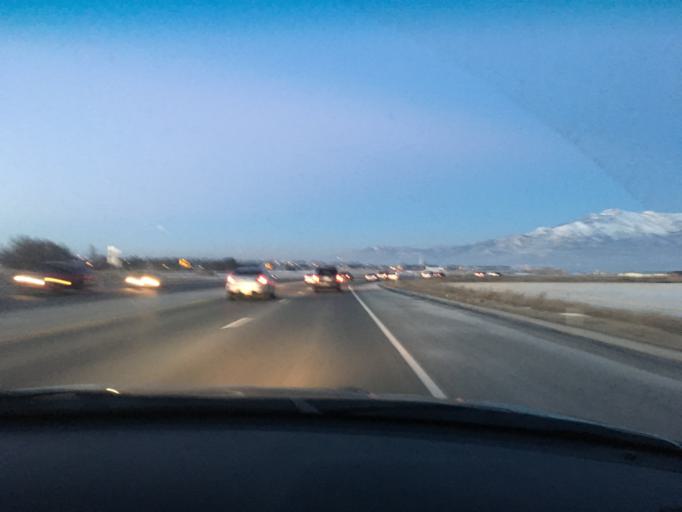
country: US
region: Utah
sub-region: Utah County
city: Saratoga Springs
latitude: 40.3858
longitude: -111.9290
